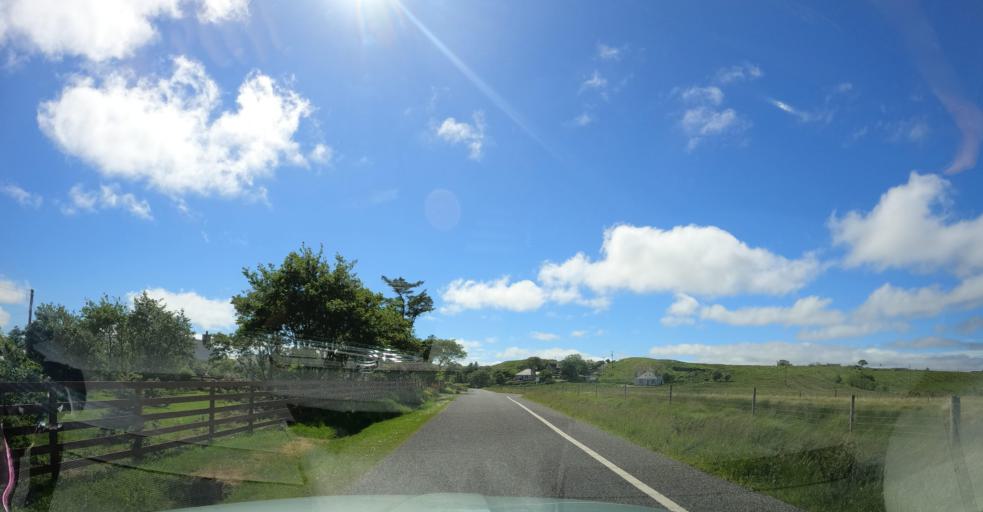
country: GB
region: Scotland
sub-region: Eilean Siar
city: Harris
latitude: 58.1980
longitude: -6.7384
